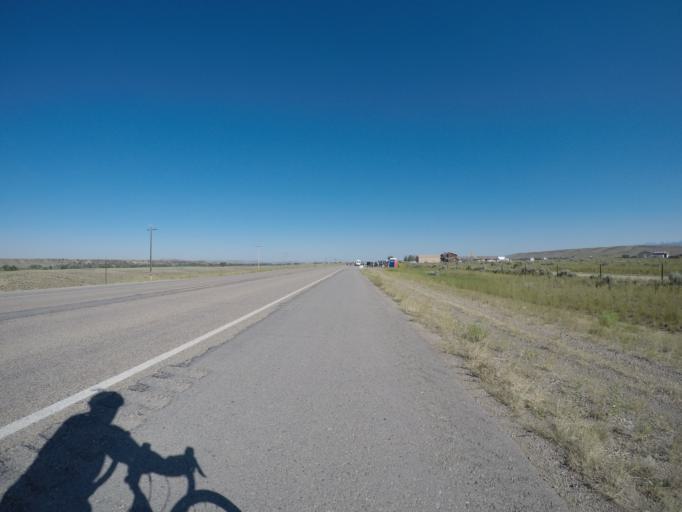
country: US
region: Wyoming
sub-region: Sublette County
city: Pinedale
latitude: 42.7645
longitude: -109.7395
